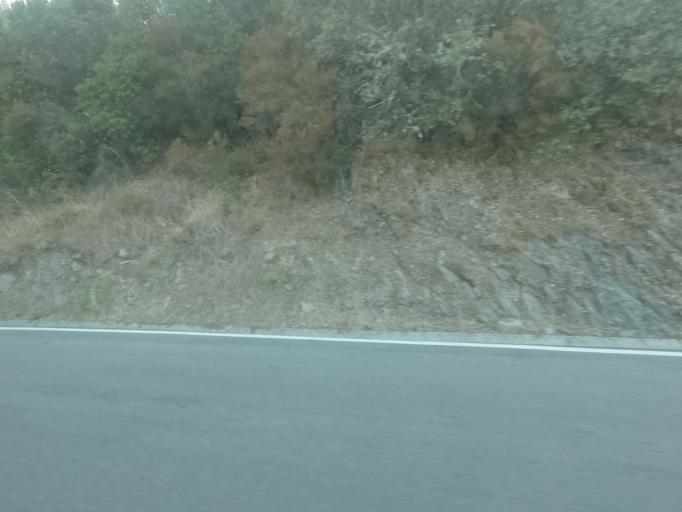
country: PT
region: Viseu
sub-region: Tabuaco
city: Tabuaco
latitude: 41.1490
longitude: -7.6208
